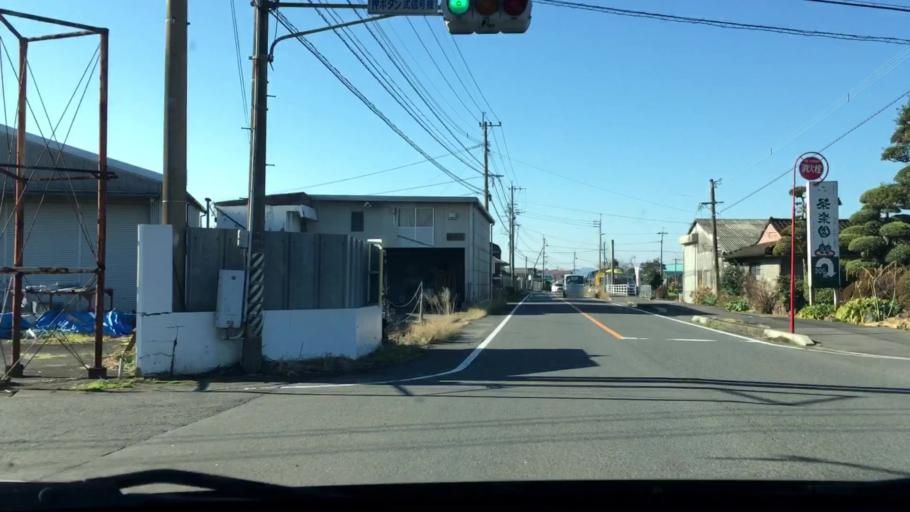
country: JP
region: Kagoshima
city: Kajiki
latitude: 31.7916
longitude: 130.7148
